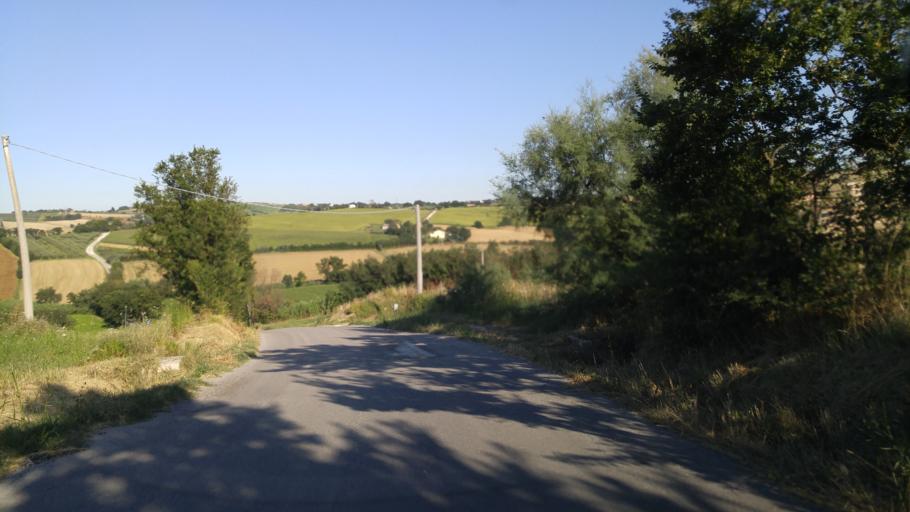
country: IT
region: The Marches
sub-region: Provincia di Pesaro e Urbino
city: Mombaroccio
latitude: 43.8118
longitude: 12.8769
